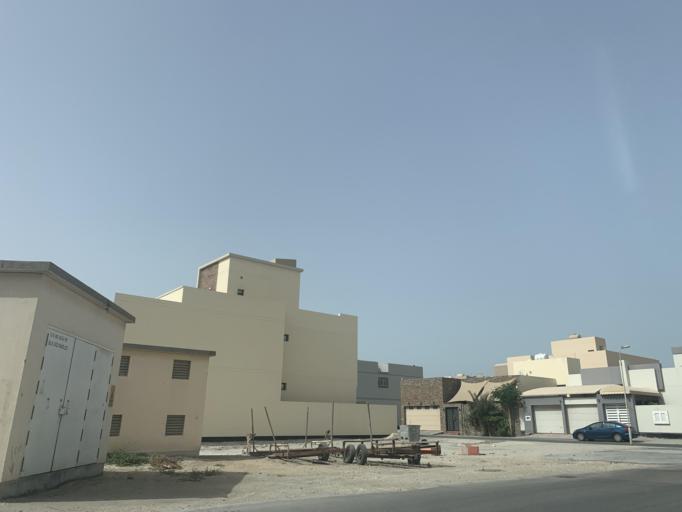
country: BH
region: Northern
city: Sitrah
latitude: 26.1711
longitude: 50.6202
